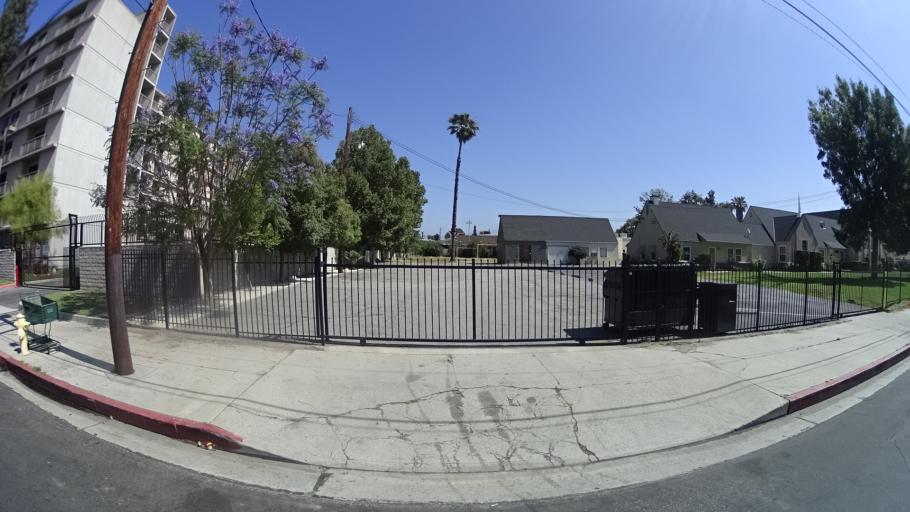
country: US
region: California
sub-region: Los Angeles County
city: Van Nuys
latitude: 34.2332
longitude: -118.4490
